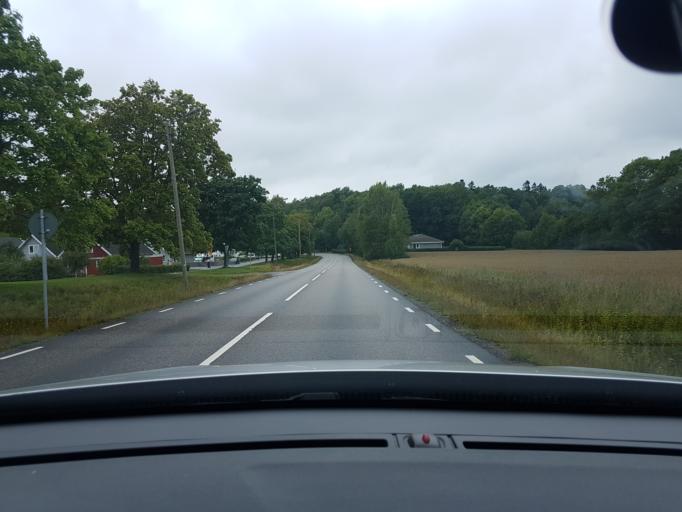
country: SE
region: Vaestra Goetaland
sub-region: Ale Kommun
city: Salanda
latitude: 57.9835
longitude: 12.2216
